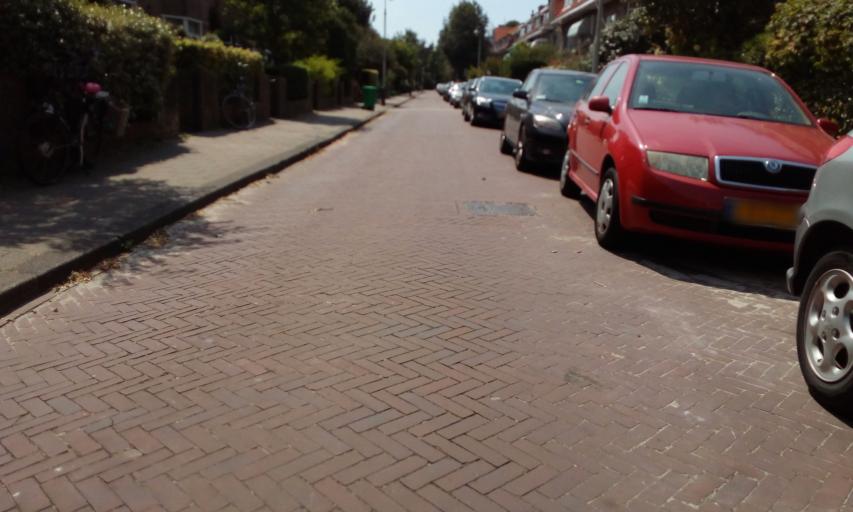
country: NL
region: South Holland
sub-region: Gemeente Den Haag
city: The Hague
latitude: 52.0912
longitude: 4.3251
